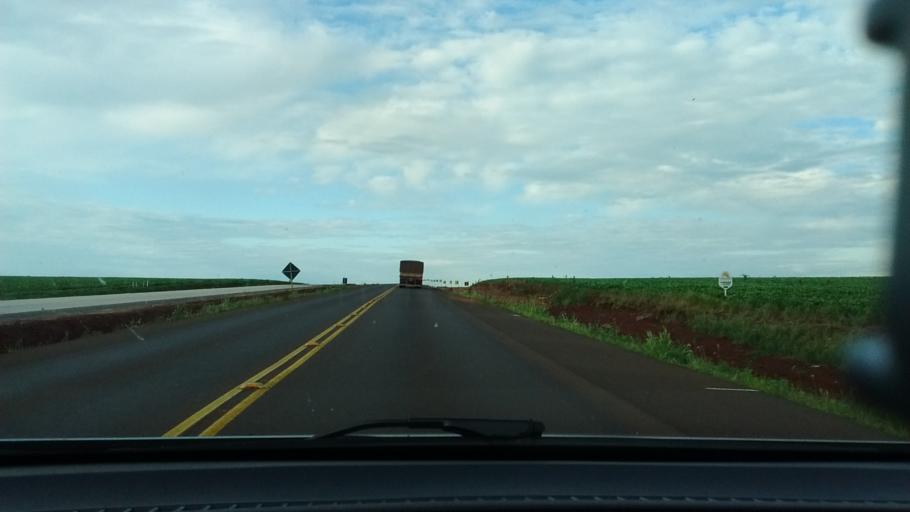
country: BR
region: Parana
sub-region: Cascavel
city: Cascavel
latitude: -25.0666
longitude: -53.5695
